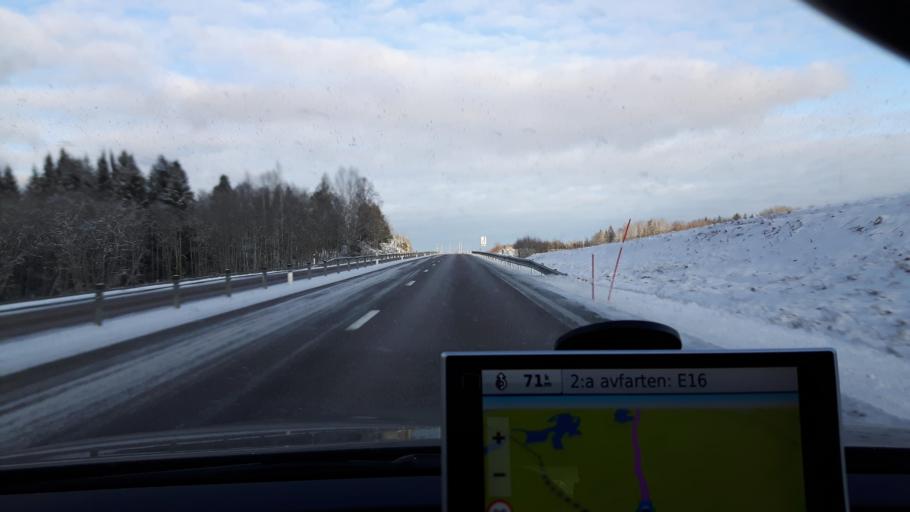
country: SE
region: Vaermland
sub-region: Karlstads Kommun
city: Edsvalla
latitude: 59.5308
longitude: 13.2118
